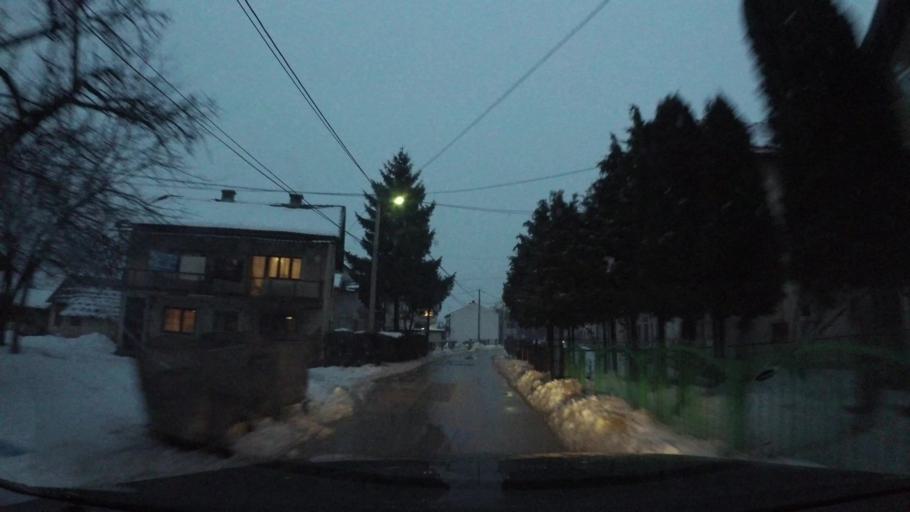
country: BA
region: Federation of Bosnia and Herzegovina
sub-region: Kanton Sarajevo
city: Sarajevo
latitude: 43.8382
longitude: 18.3052
